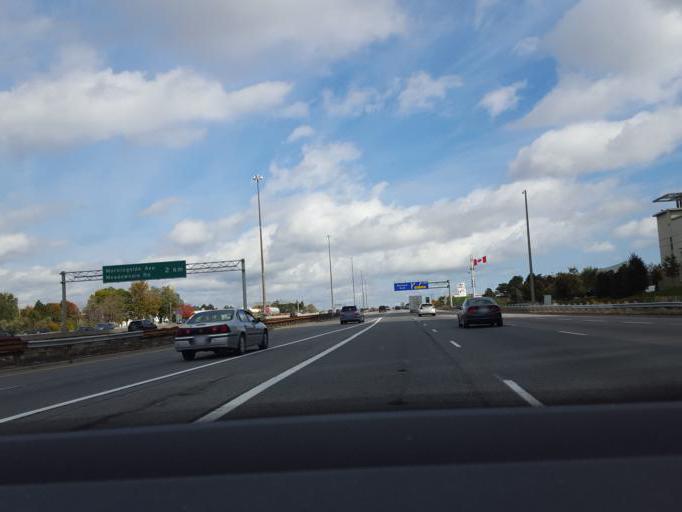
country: CA
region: Ontario
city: Scarborough
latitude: 43.7822
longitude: -79.2473
